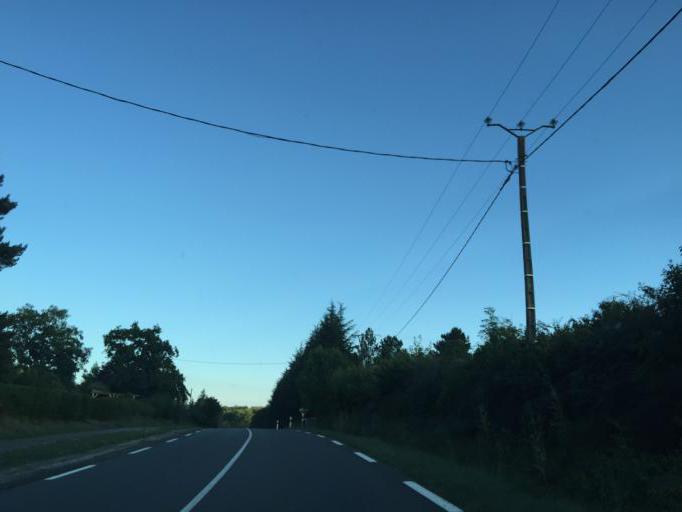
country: FR
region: Midi-Pyrenees
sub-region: Departement de l'Aveyron
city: Sebazac-Concoures
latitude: 44.3945
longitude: 2.5633
